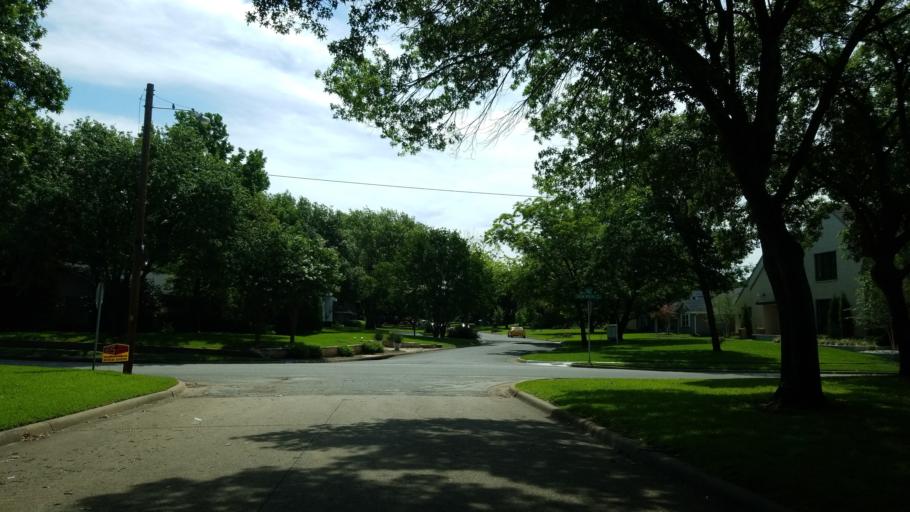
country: US
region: Texas
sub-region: Dallas County
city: Farmers Branch
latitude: 32.9070
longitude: -96.8437
